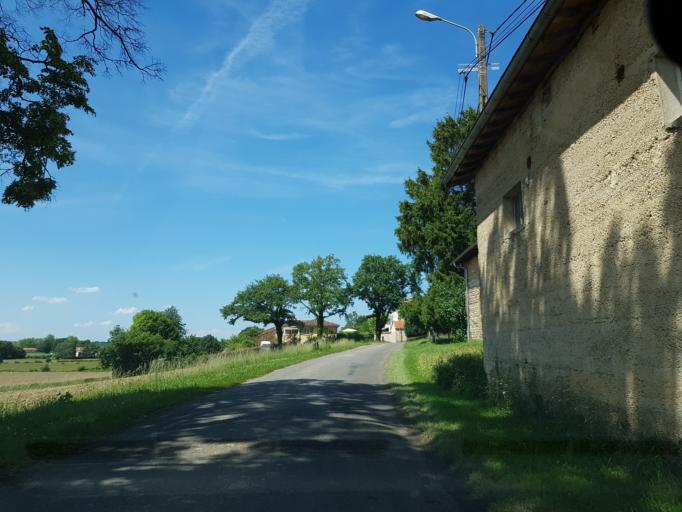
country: FR
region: Rhone-Alpes
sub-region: Departement de l'Ain
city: Montagnat
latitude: 46.1889
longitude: 5.2785
